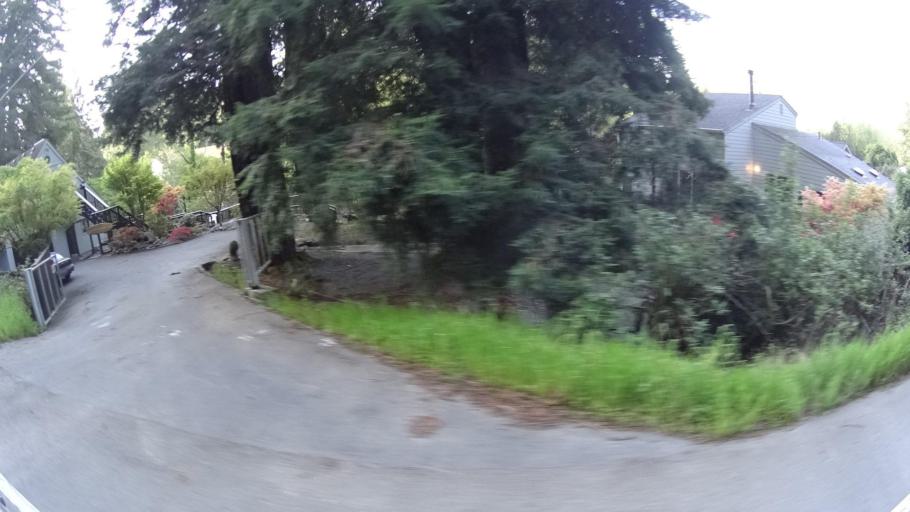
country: US
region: California
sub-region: Humboldt County
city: Myrtletown
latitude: 40.7601
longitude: -124.0533
